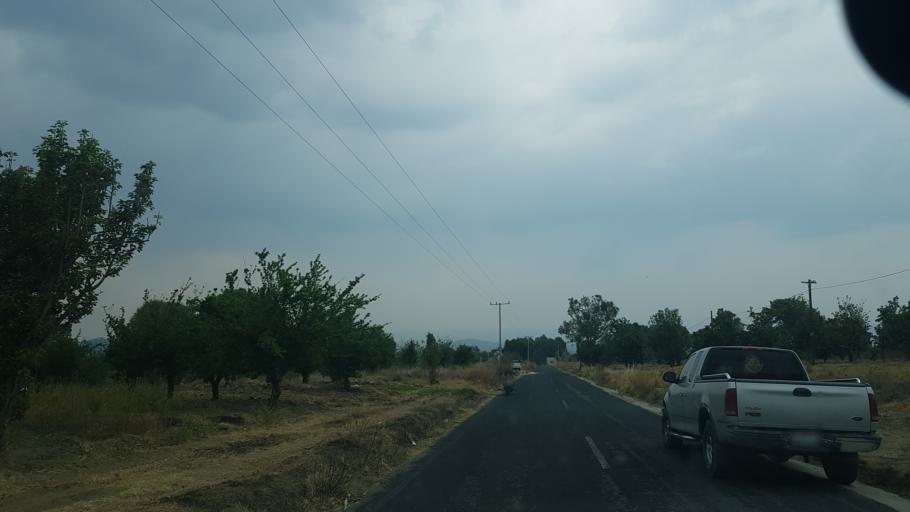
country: MX
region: Puebla
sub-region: Chiautzingo
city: San Nicolas Zecalacoayan
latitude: 19.1854
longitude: -98.4789
